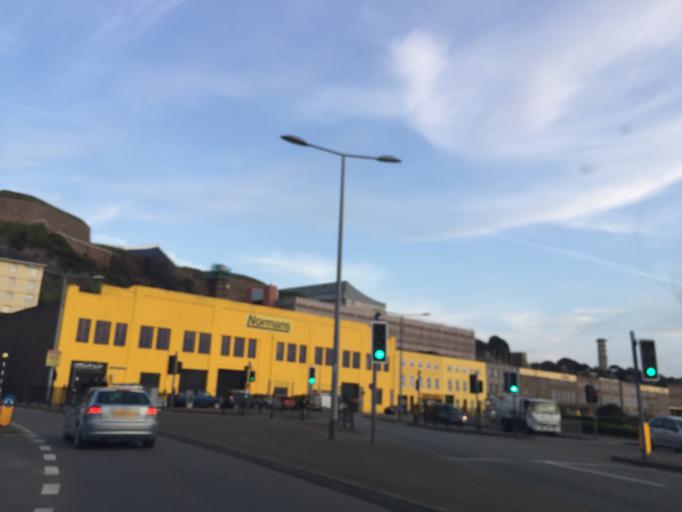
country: JE
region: St Helier
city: Saint Helier
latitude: 49.1821
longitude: -2.1088
